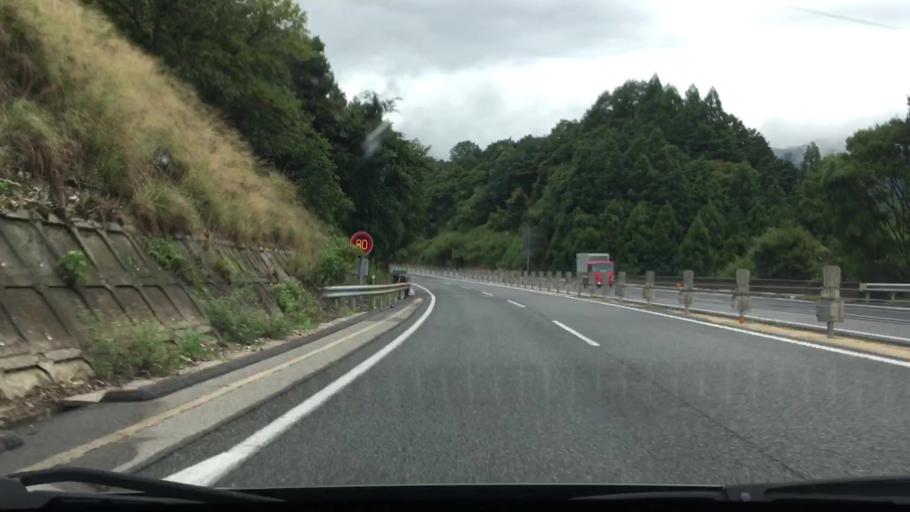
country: JP
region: Hiroshima
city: Hiroshima-shi
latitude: 34.5583
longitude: 132.4503
